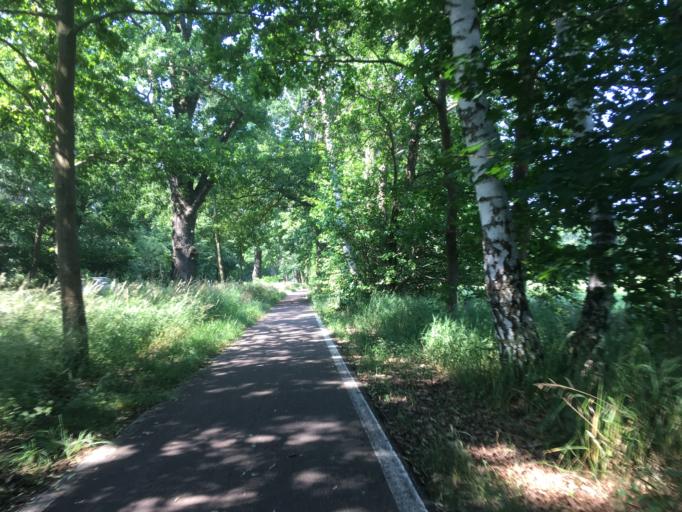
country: DE
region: Saxony-Anhalt
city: Dessau
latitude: 51.8053
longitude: 12.2034
